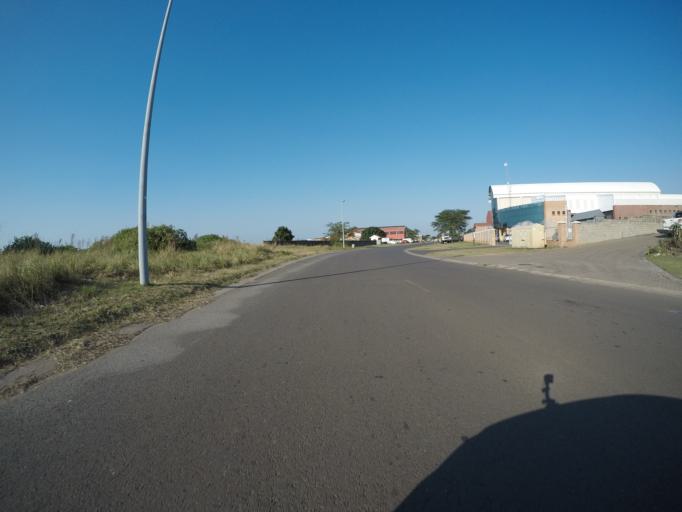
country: ZA
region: KwaZulu-Natal
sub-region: uThungulu District Municipality
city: Richards Bay
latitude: -28.7369
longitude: 32.0396
